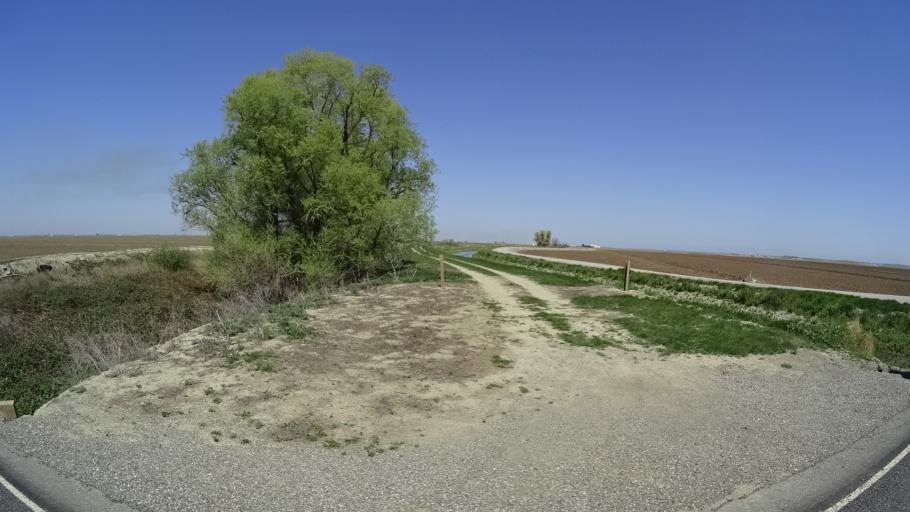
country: US
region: California
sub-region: Glenn County
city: Willows
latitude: 39.4581
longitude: -122.0857
